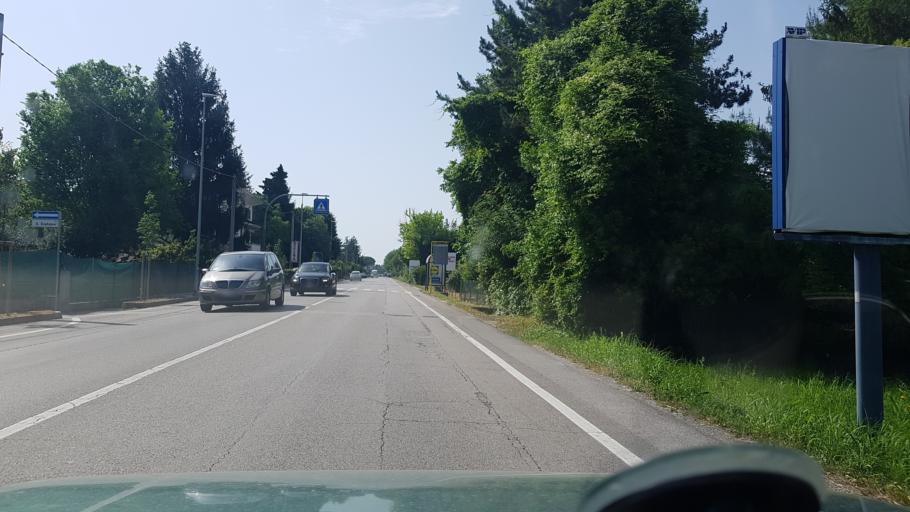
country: IT
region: Friuli Venezia Giulia
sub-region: Provincia di Gorizia
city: Ronchi dei Legionari
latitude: 45.8370
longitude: 13.4956
